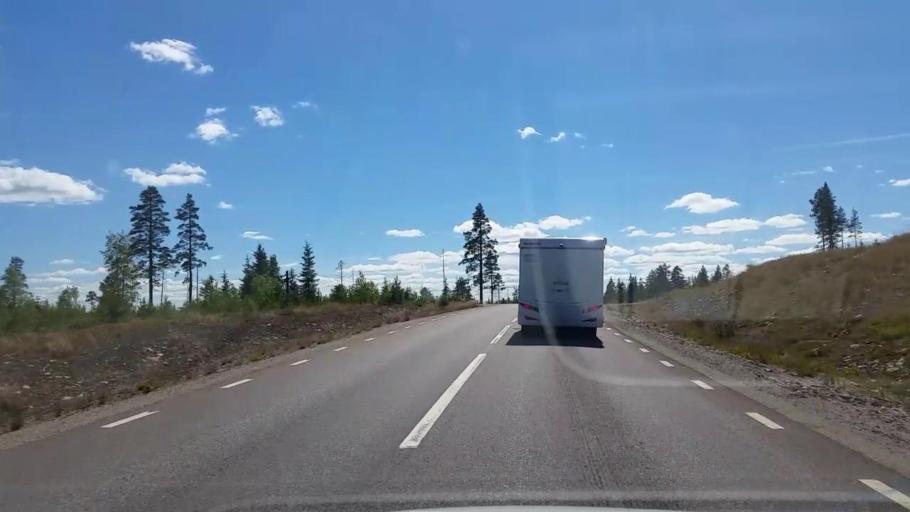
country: SE
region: Gaevleborg
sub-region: Bollnas Kommun
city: Vittsjo
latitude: 61.1028
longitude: 15.8558
